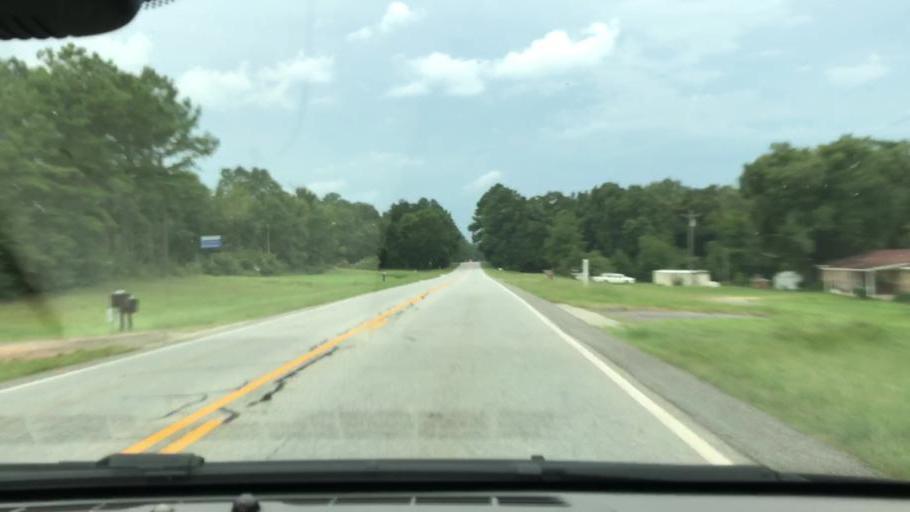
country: US
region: Georgia
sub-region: Early County
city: Blakely
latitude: 31.2802
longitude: -85.0833
